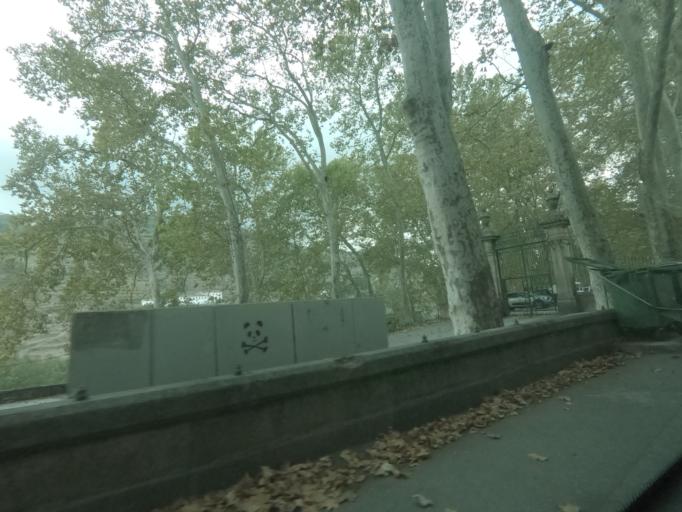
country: PT
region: Vila Real
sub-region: Mesao Frio
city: Mesao Frio
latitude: 41.1942
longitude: -7.8994
